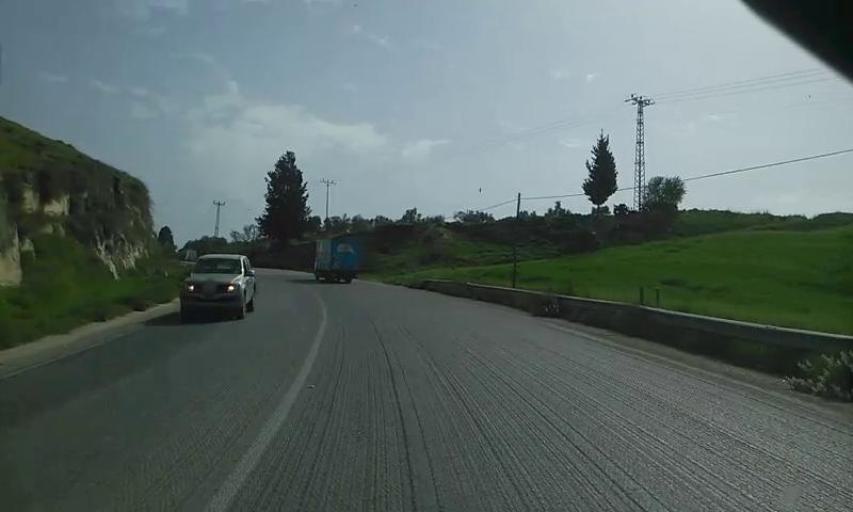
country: PS
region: West Bank
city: `Anzah
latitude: 32.3811
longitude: 35.2146
